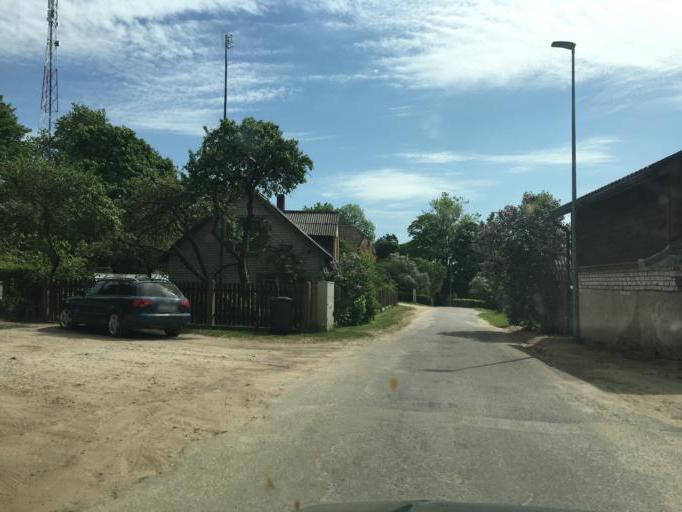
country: LV
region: Talsu Rajons
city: Valdemarpils
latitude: 57.3694
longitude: 22.5938
